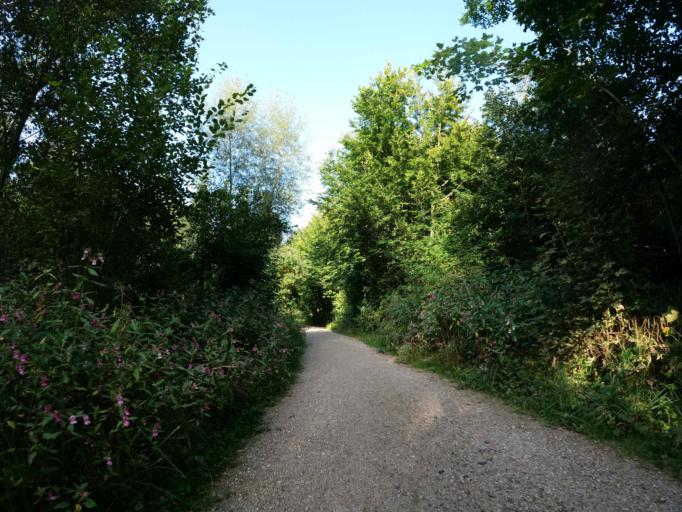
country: DE
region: Bavaria
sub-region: Upper Bavaria
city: Germering
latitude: 48.1690
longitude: 11.4003
